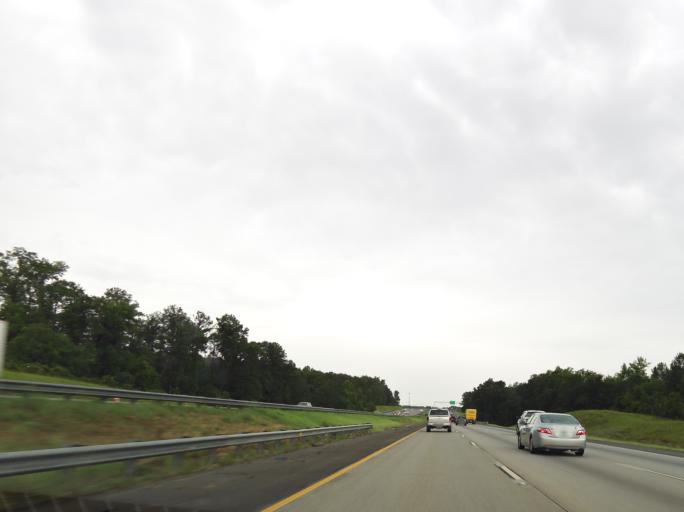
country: US
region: Georgia
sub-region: Houston County
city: Centerville
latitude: 32.5577
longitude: -83.7443
